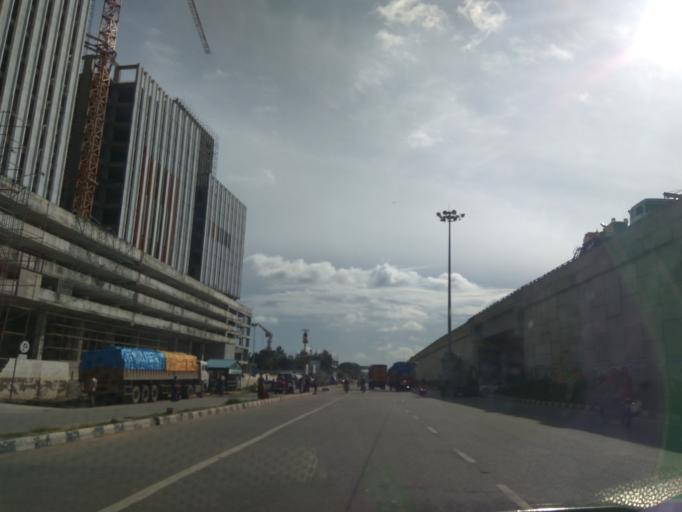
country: IN
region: Karnataka
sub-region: Bangalore Rural
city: Hoskote
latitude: 13.0533
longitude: 77.7613
